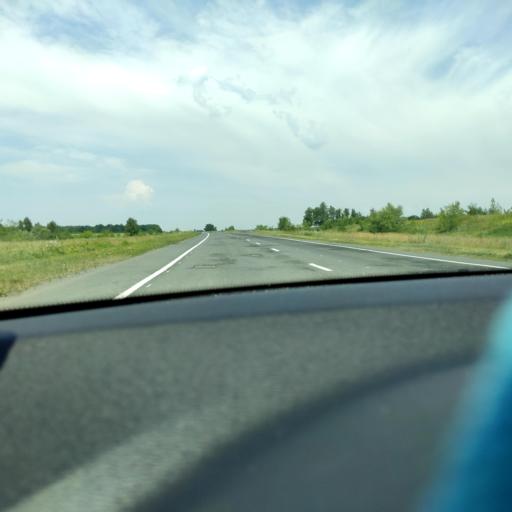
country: RU
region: Samara
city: Petra-Dubrava
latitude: 53.3140
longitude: 50.4237
